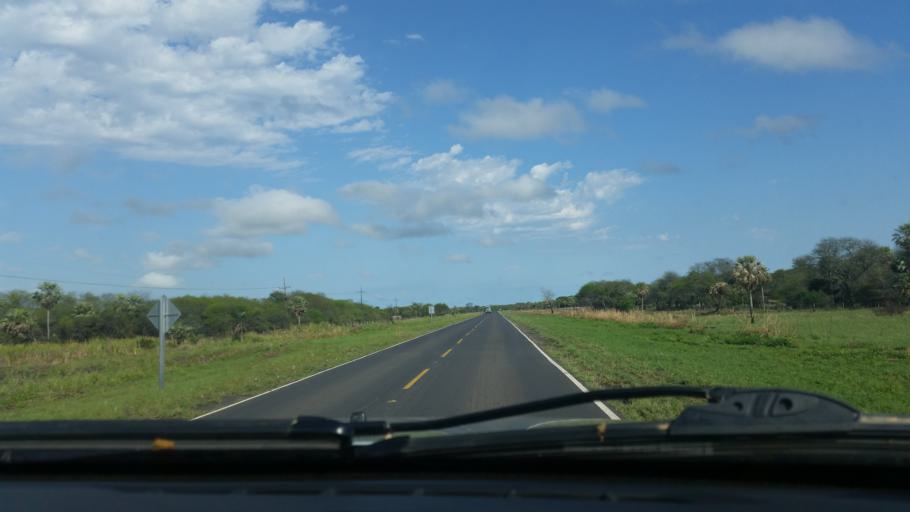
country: PY
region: Presidente Hayes
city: Benjamin Aceval
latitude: -24.9099
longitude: -57.6338
